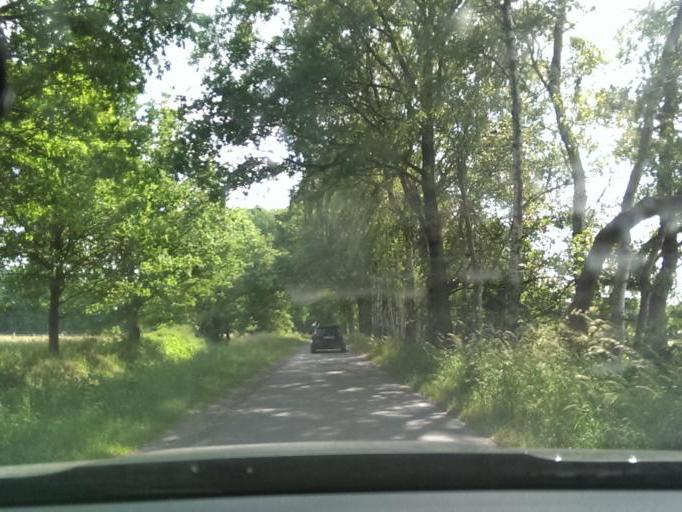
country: DE
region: Lower Saxony
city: Lindwedel
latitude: 52.5364
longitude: 9.6630
